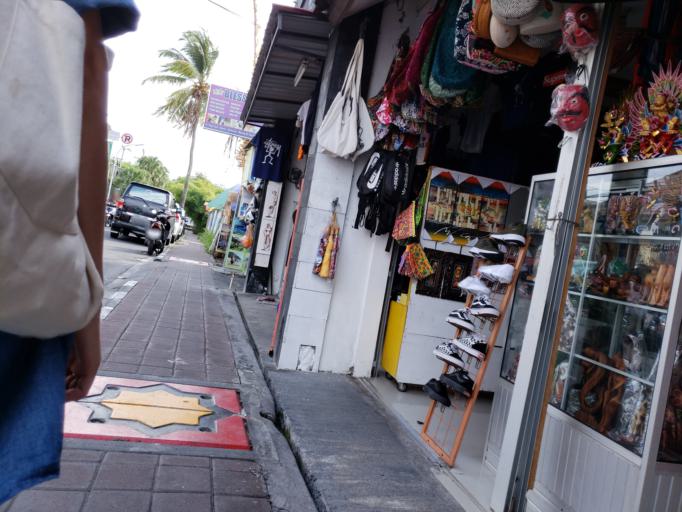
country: ID
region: Bali
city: Kuta
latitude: -8.6851
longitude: 115.1567
